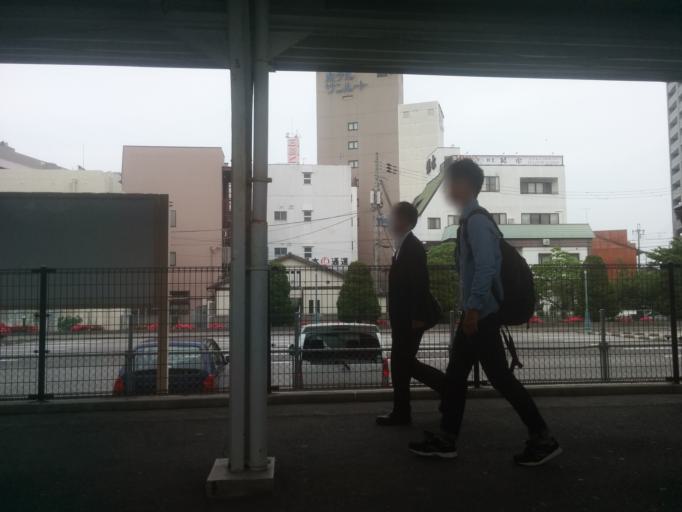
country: JP
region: Shiga Prefecture
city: Hikone
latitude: 35.2727
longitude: 136.2634
